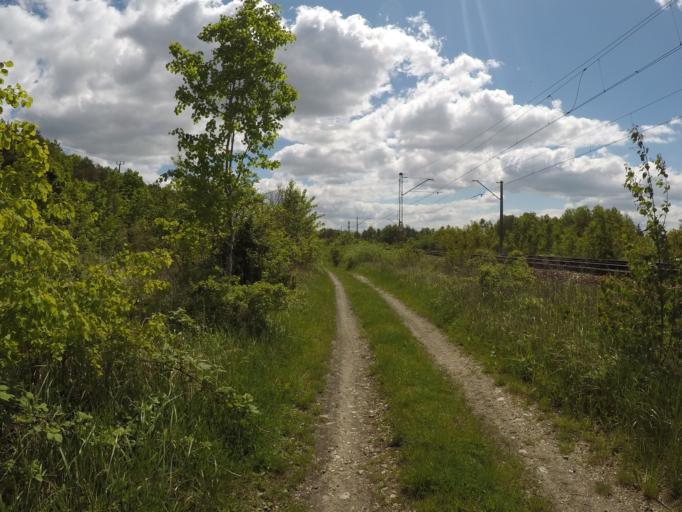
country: PL
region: Swietokrzyskie
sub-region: Powiat kielecki
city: Kostomloty Pierwsze
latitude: 50.9298
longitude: 20.6029
